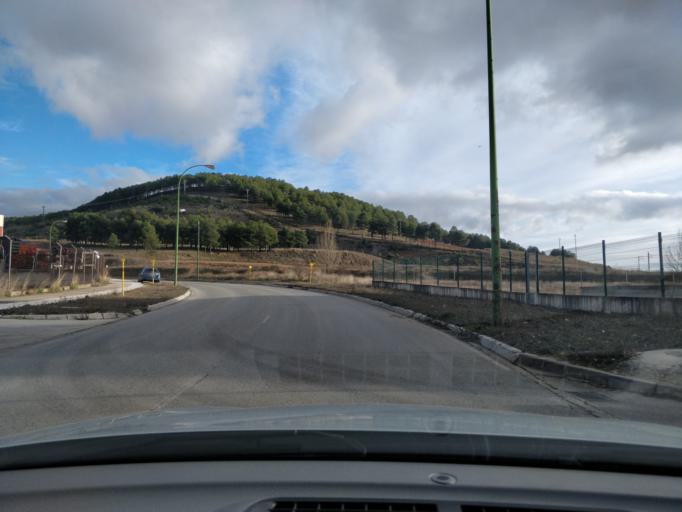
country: ES
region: Castille and Leon
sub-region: Provincia de Burgos
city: Villalbilla de Burgos
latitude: 42.3634
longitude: -3.7515
